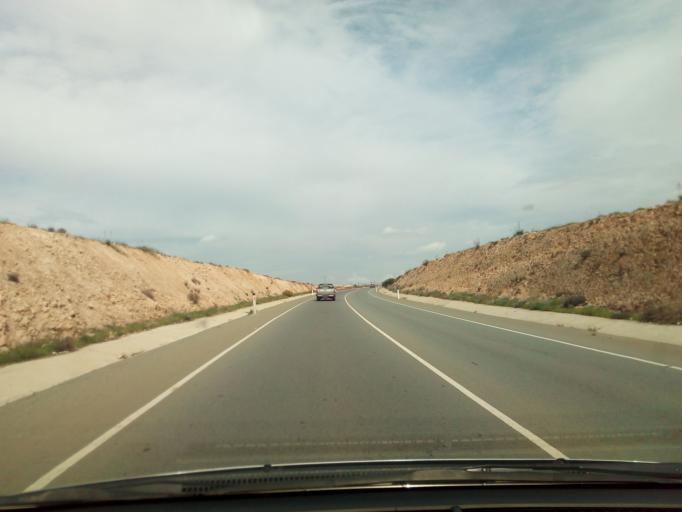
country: CY
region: Lefkosia
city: Akaki
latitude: 35.1582
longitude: 33.1573
